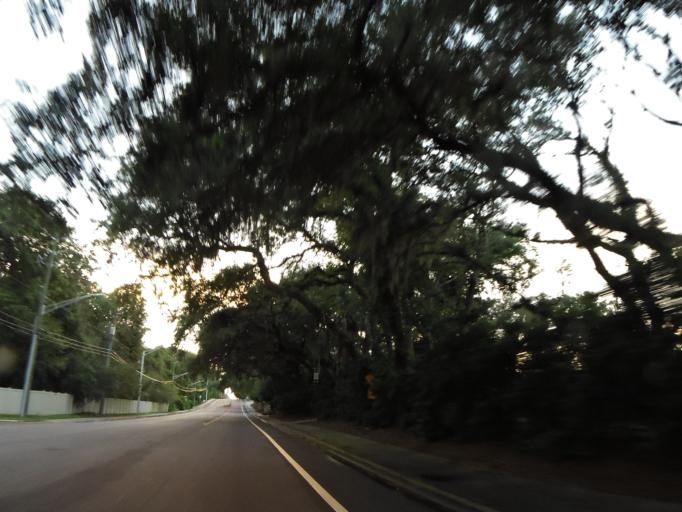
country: US
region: Florida
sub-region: Duval County
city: Jacksonville
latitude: 30.3669
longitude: -81.5639
